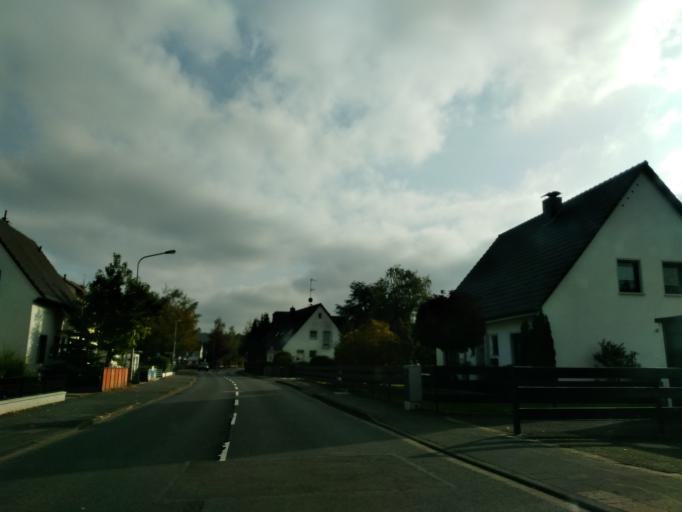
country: DE
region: North Rhine-Westphalia
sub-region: Regierungsbezirk Koln
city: Konigswinter
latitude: 50.7052
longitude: 7.1808
